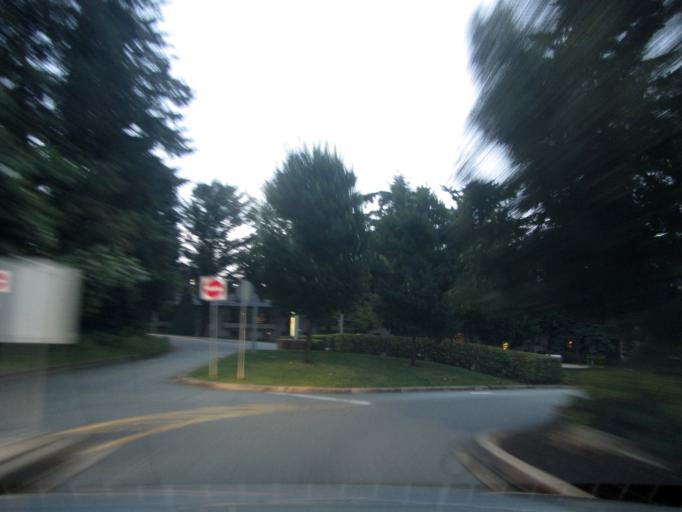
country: US
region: Washington
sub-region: Whatcom County
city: Sumas
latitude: 49.0376
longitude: -122.3124
